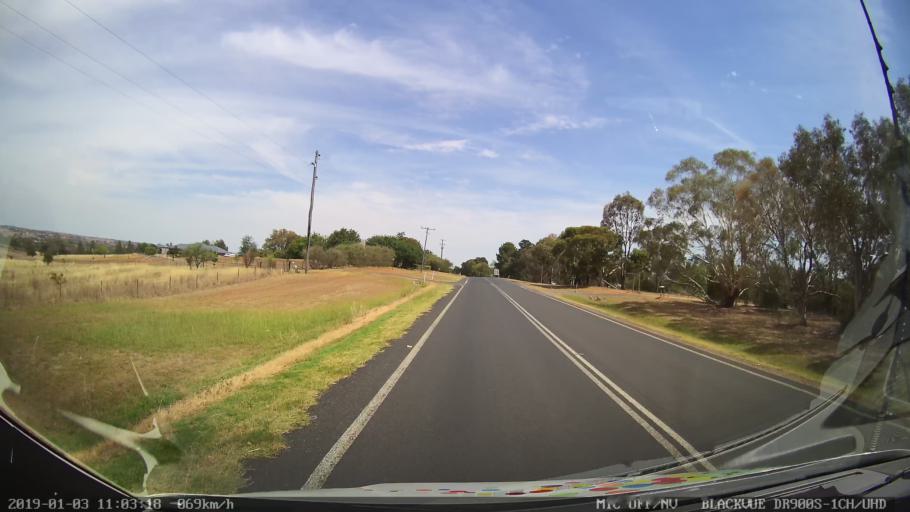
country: AU
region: New South Wales
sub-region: Young
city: Young
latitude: -34.2916
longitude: 148.2956
